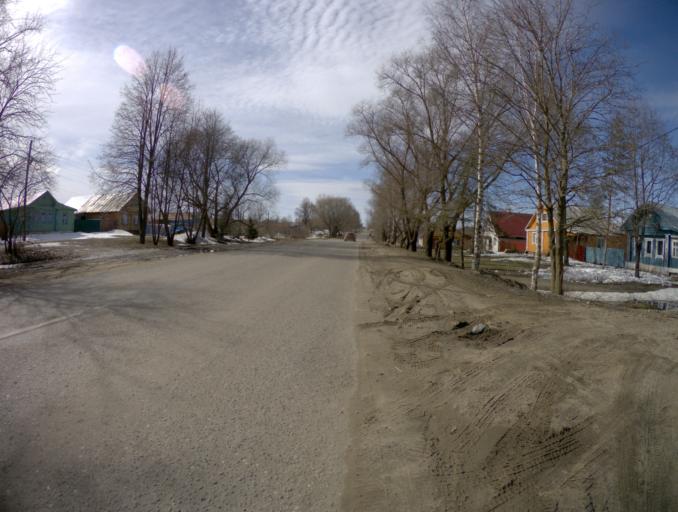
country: RU
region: Vladimir
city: Suzdal'
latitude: 56.4273
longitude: 40.4223
